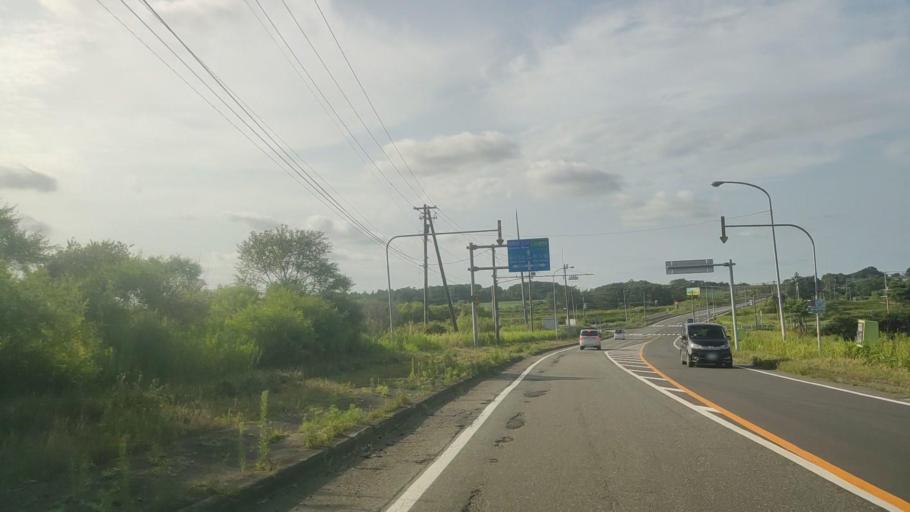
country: JP
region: Hokkaido
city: Chitose
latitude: 42.8841
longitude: 141.8126
